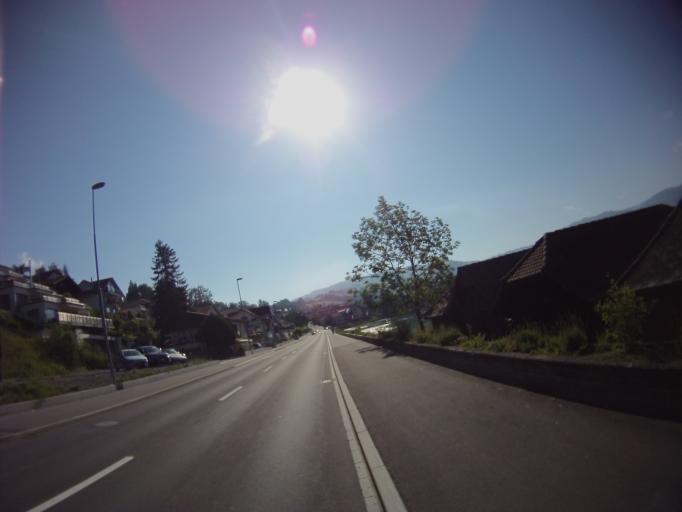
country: CH
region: Zug
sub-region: Zug
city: Unterageri
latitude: 47.1374
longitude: 8.6013
